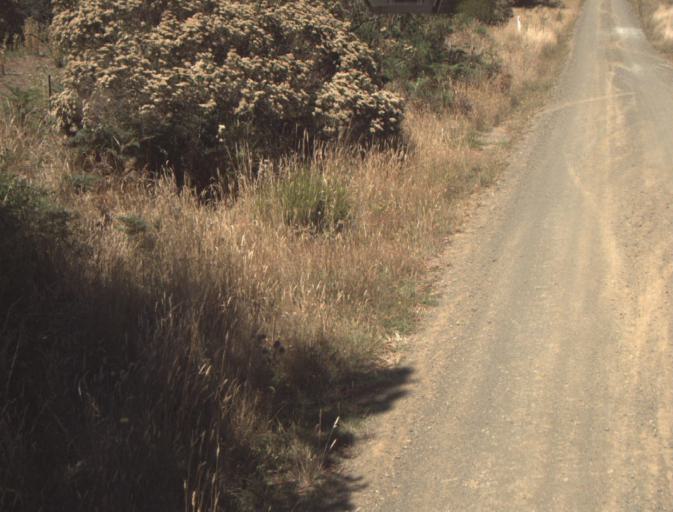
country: AU
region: Tasmania
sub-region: Launceston
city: Newstead
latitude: -41.3531
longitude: 147.3795
